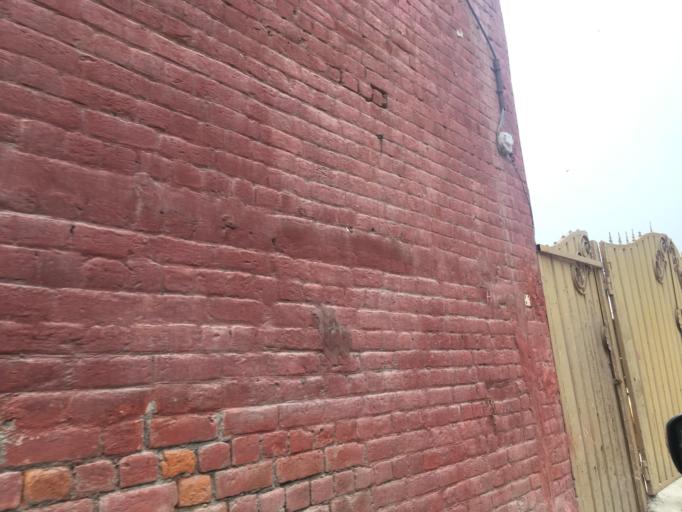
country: PK
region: Punjab
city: Lahore
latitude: 31.6220
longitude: 74.3468
